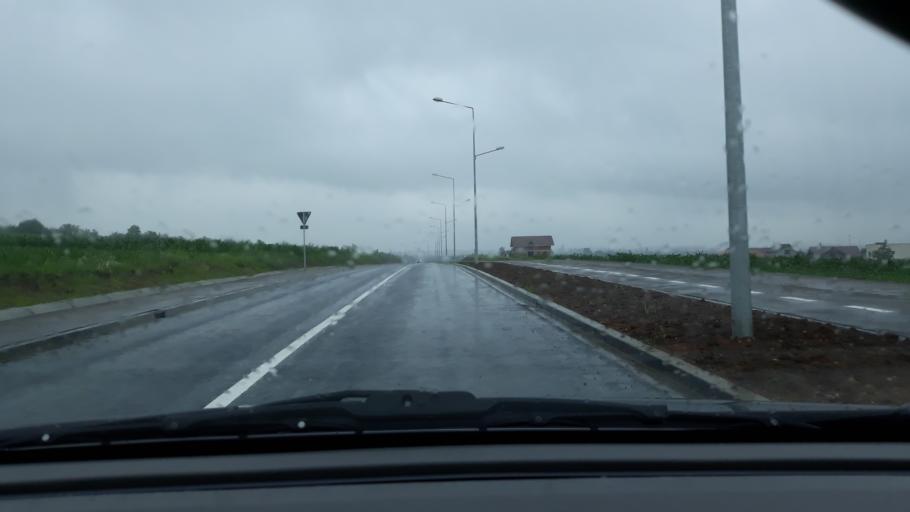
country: RO
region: Bihor
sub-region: Comuna Biharea
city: Biharea
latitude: 47.1079
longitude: 21.9065
